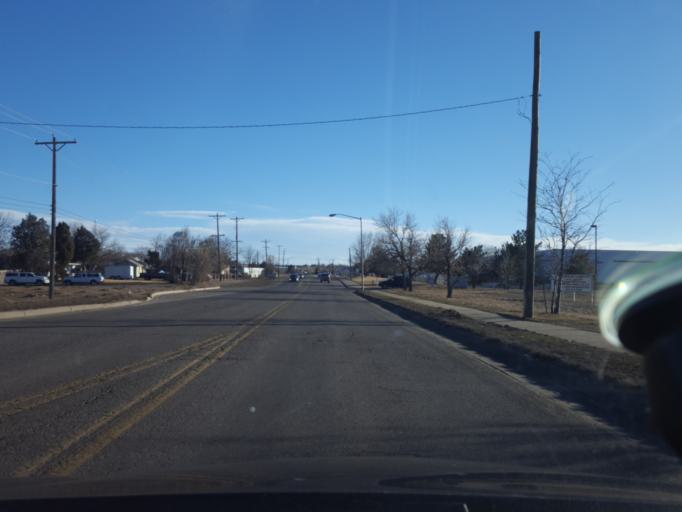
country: US
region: Colorado
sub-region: Adams County
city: Aurora
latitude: 39.7449
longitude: -104.7725
